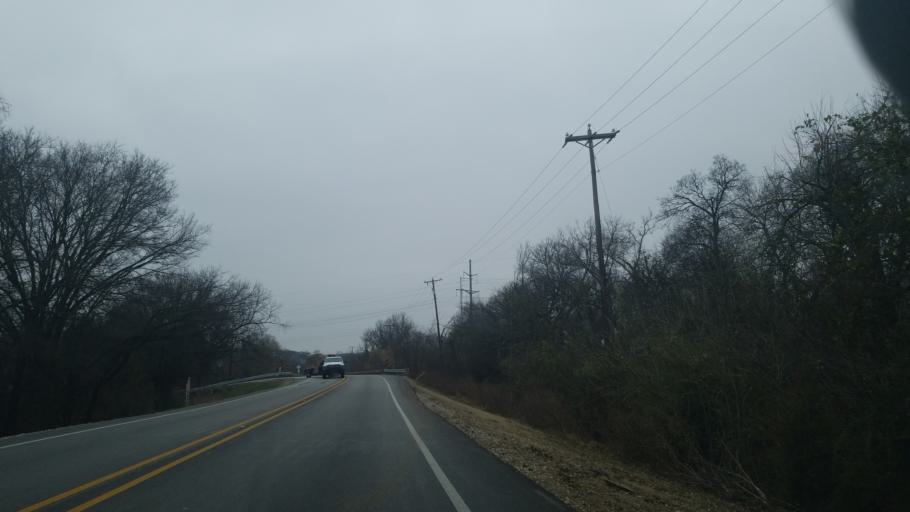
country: US
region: Texas
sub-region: Denton County
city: Argyle
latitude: 33.1529
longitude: -97.1419
